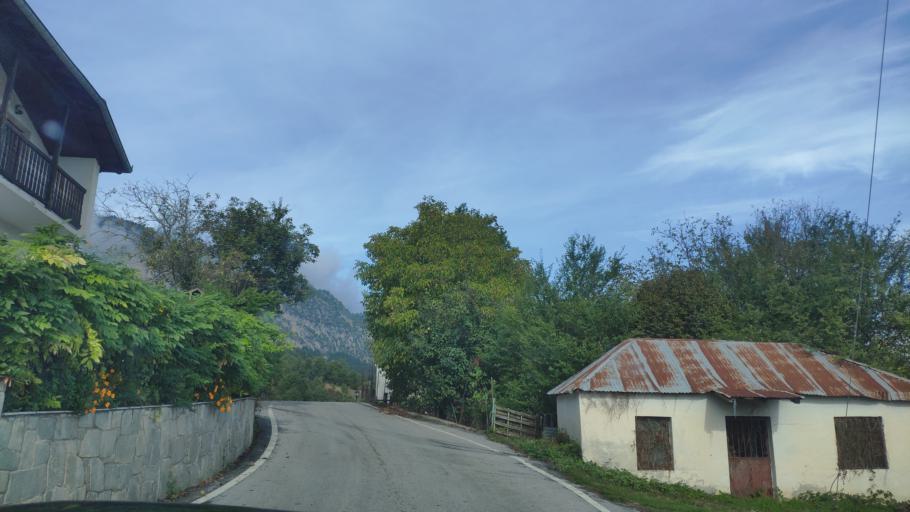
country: GR
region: West Macedonia
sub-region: Nomos Kastorias
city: Nestorio
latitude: 40.2756
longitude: 20.9756
